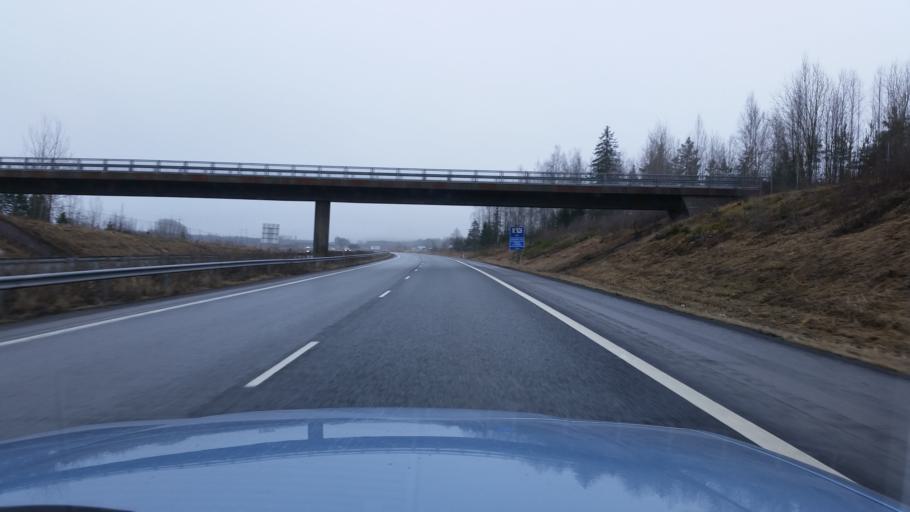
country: FI
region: Pirkanmaa
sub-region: Etelae-Pirkanmaa
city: Toijala
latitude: 61.1969
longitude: 23.8501
